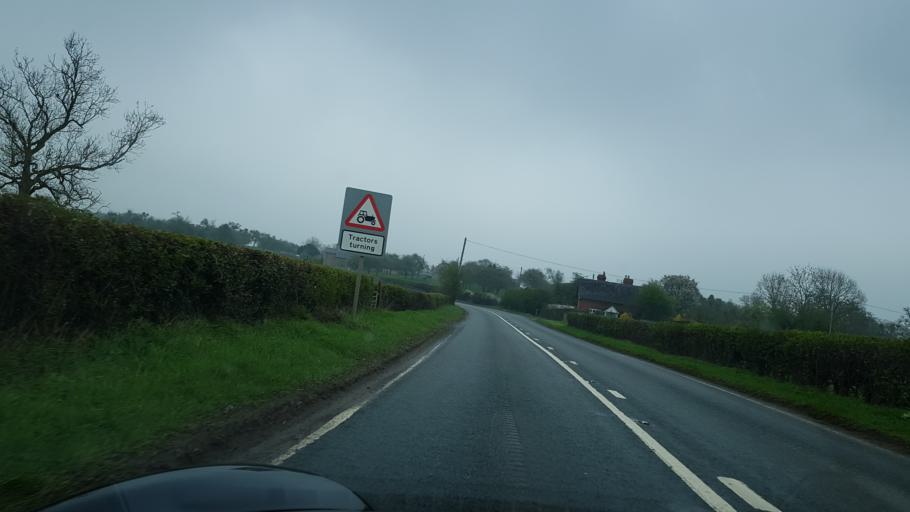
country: GB
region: England
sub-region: Herefordshire
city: Yatton
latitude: 51.9986
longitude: -2.4996
